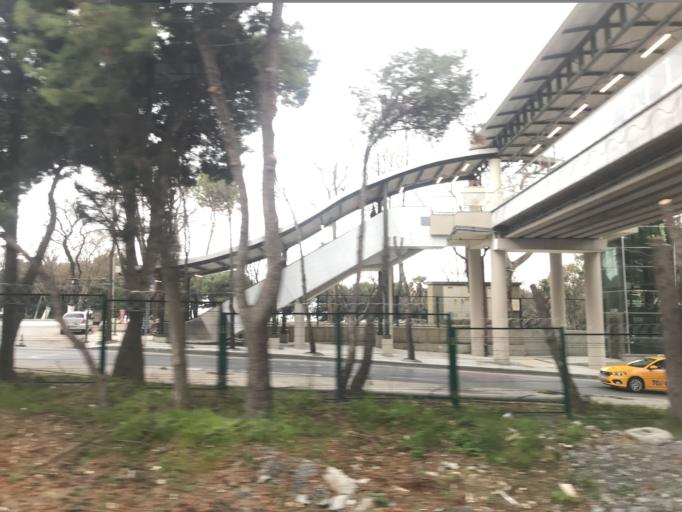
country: TR
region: Istanbul
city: Bahcelievler
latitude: 40.9678
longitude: 28.7968
